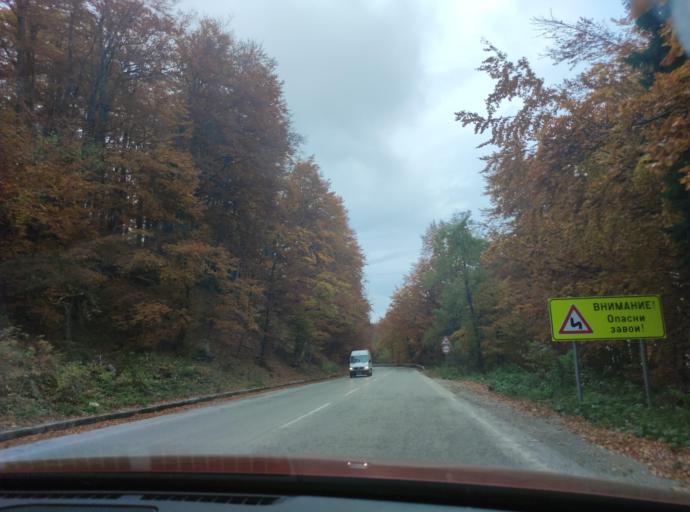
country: BG
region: Montana
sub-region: Obshtina Berkovitsa
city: Berkovitsa
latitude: 43.1273
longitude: 23.1361
